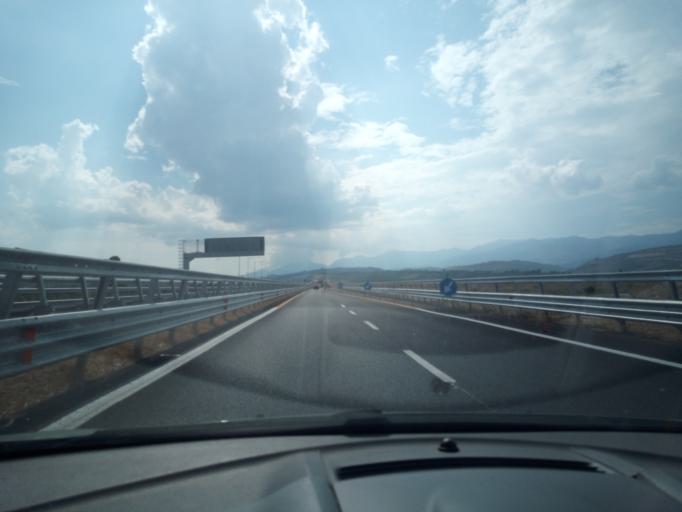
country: IT
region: Calabria
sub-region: Provincia di Cosenza
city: San Lorenzo del Vallo
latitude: 39.7237
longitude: 16.2530
